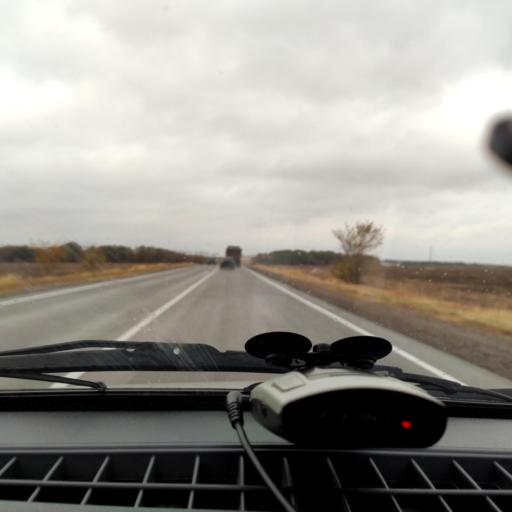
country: RU
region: Voronezj
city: Strelitsa
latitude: 51.5138
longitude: 38.9672
